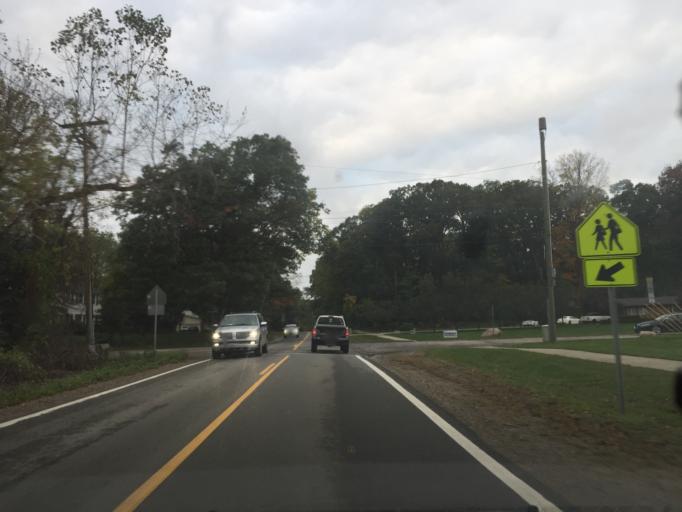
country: US
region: Michigan
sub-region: Oakland County
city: Franklin
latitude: 42.5586
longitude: -83.2947
